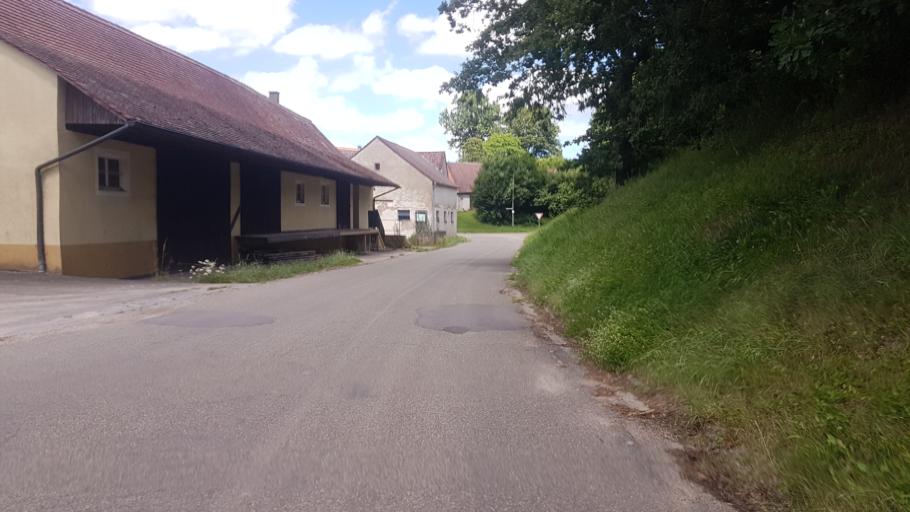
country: DE
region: Bavaria
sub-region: Regierungsbezirk Mittelfranken
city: Colmberg
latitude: 49.3360
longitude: 10.3759
